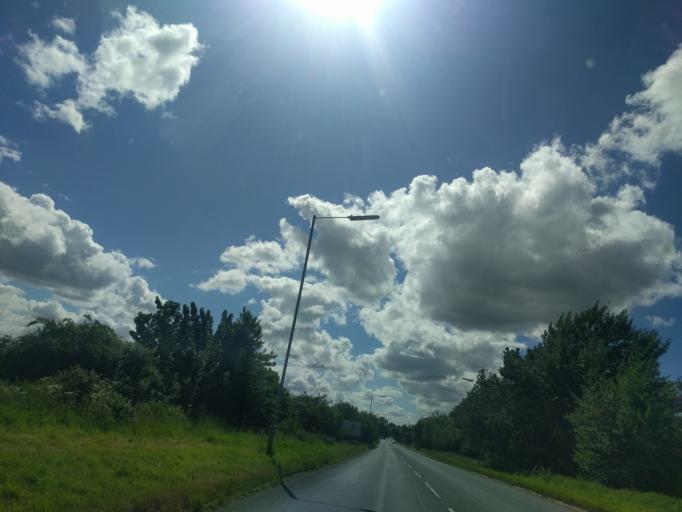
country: GB
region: England
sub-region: Wiltshire
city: Calne
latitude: 51.4278
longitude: -1.9661
